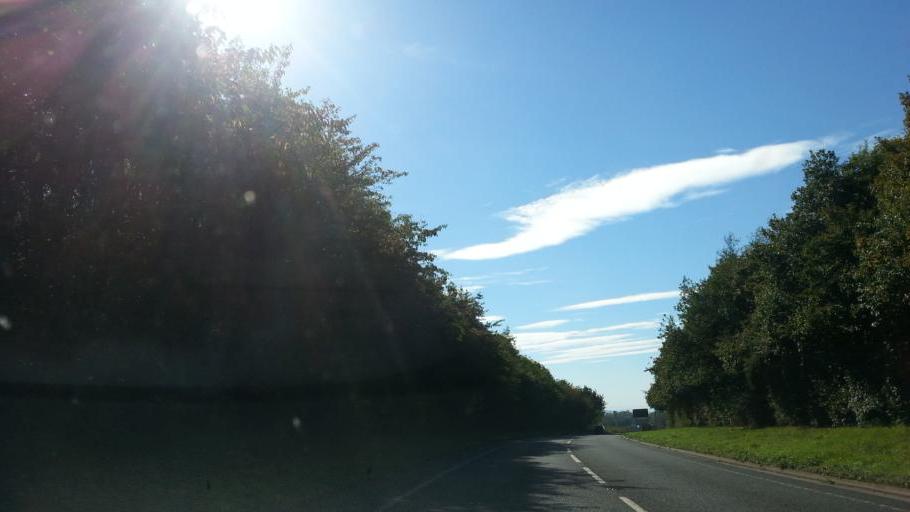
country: GB
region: England
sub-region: Telford and Wrekin
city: Newport
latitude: 52.7549
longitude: -2.3751
